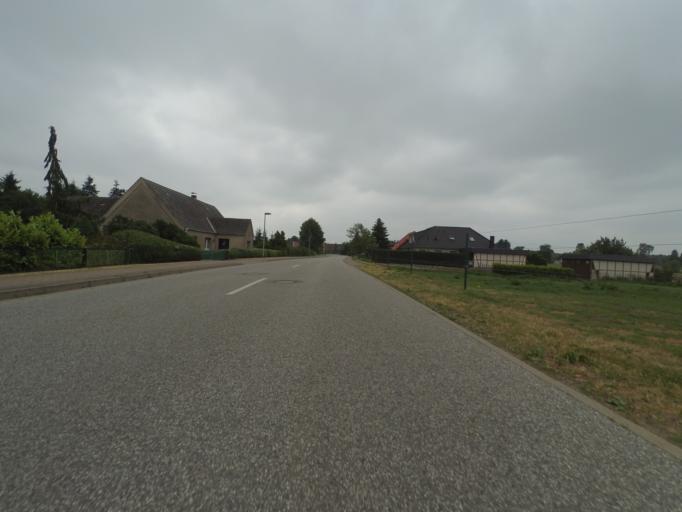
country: DE
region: Mecklenburg-Vorpommern
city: Spornitz
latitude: 53.4812
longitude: 11.6843
